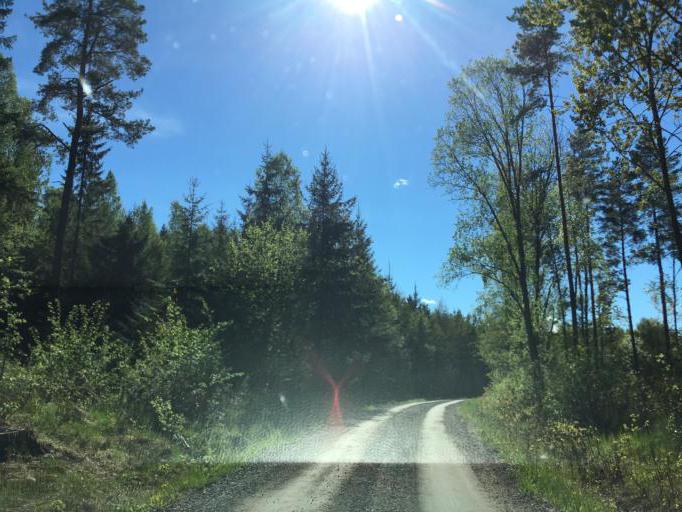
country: SE
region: Soedermanland
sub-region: Eskilstuna Kommun
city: Kvicksund
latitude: 59.3488
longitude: 16.3163
